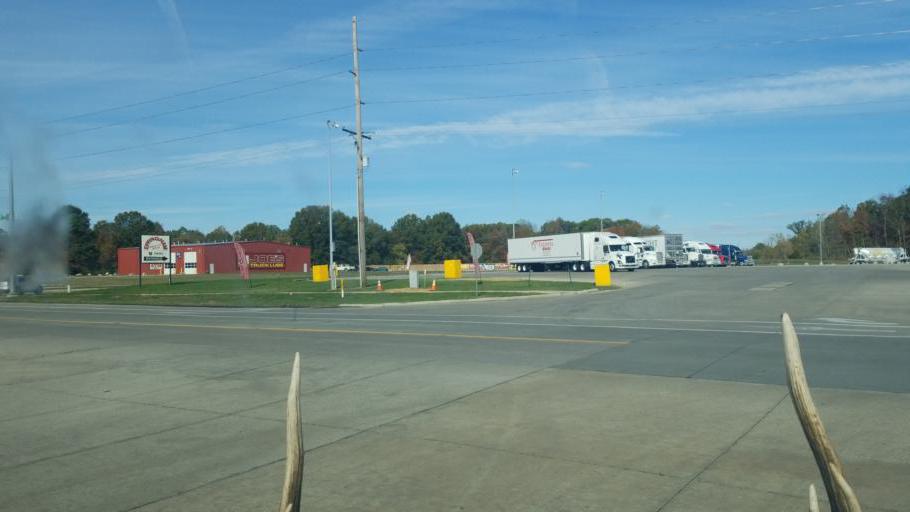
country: US
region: Illinois
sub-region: Effingham County
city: Effingham
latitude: 39.1206
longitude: -88.5732
